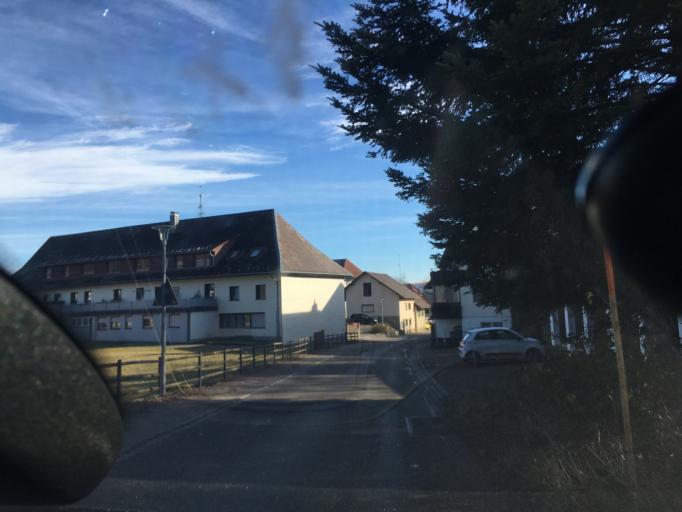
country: DE
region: Baden-Wuerttemberg
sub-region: Freiburg Region
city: Gorwihl
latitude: 47.6422
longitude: 8.0742
